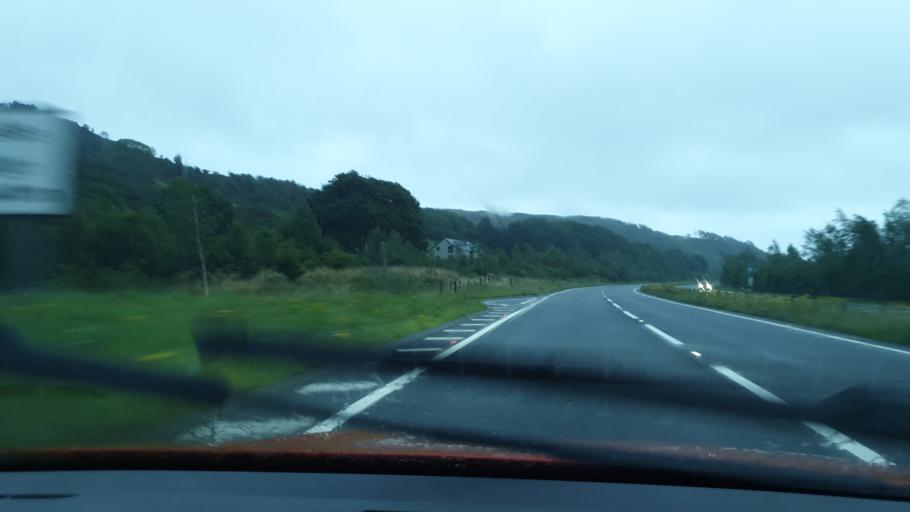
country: GB
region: England
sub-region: Cumbria
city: Grange-over-Sands
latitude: 54.2477
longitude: -2.9338
